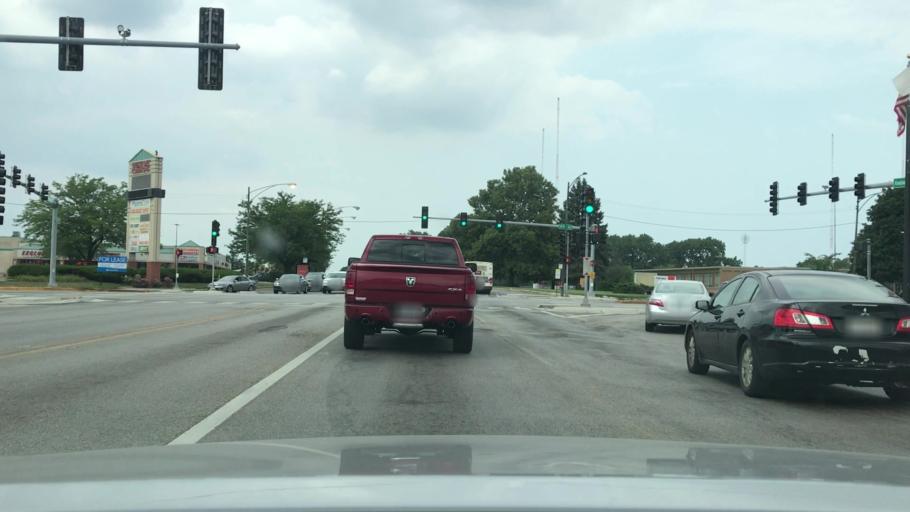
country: US
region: Illinois
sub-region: Cook County
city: Evergreen Park
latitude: 41.7347
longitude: -87.7022
